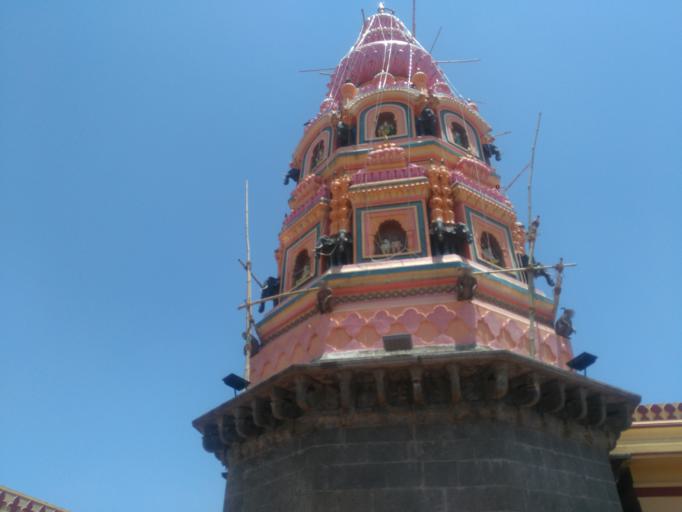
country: IN
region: Maharashtra
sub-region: Pune Division
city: Jejuri
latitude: 18.2780
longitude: 74.3175
